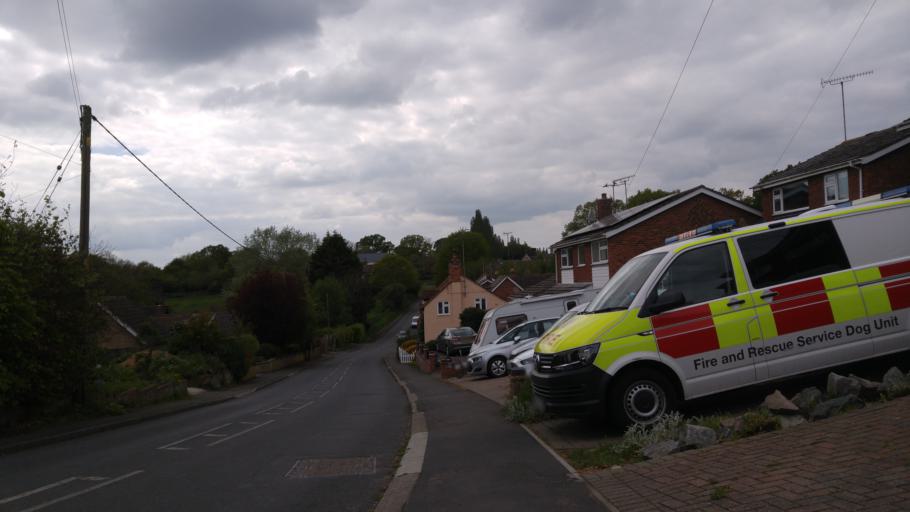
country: GB
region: England
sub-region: Essex
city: Earls Colne
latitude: 51.9414
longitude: 0.6870
